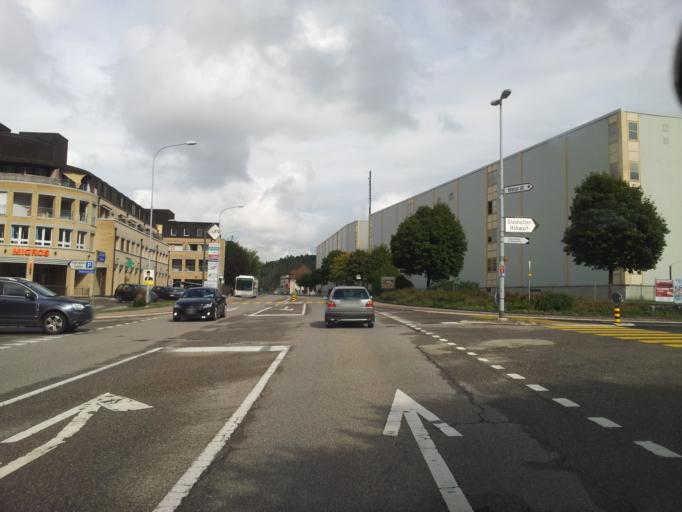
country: CH
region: Aargau
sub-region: Bezirk Zofingen
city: Fulenbach
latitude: 47.2645
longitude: 7.8284
